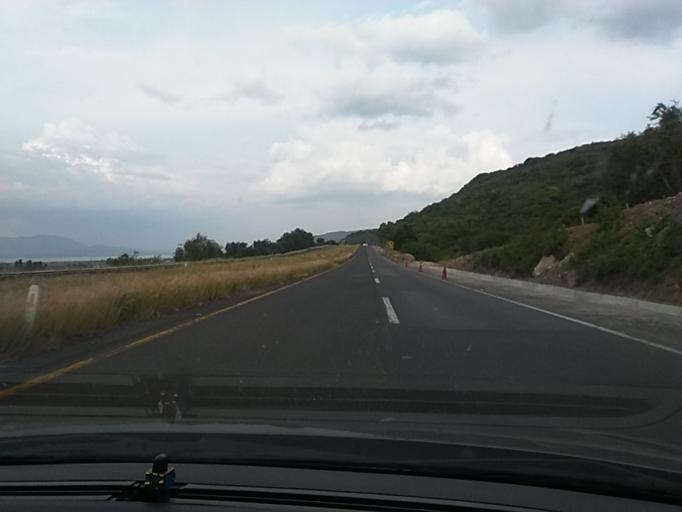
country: MX
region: Mexico
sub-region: Chapultepec
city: Chucandiro
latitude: 19.8823
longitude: -101.3471
